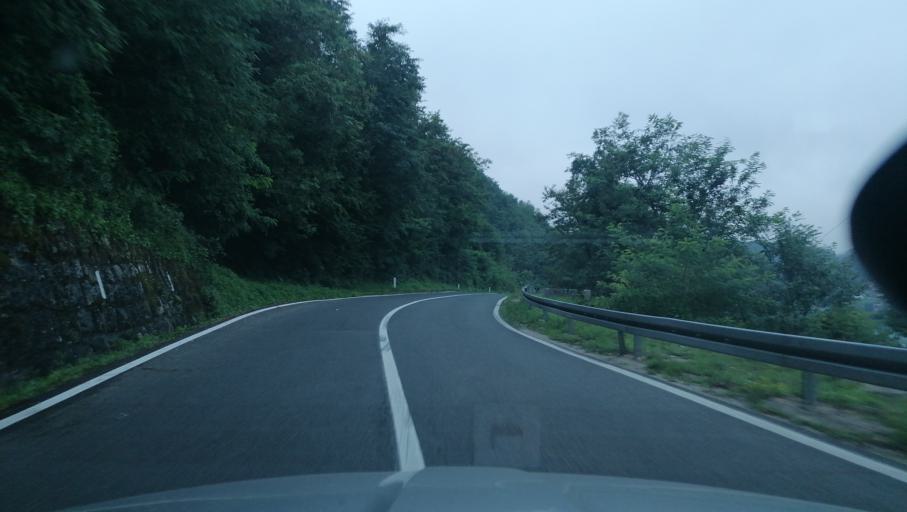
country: BA
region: Federation of Bosnia and Herzegovina
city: Jablanica
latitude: 43.7171
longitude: 17.7116
